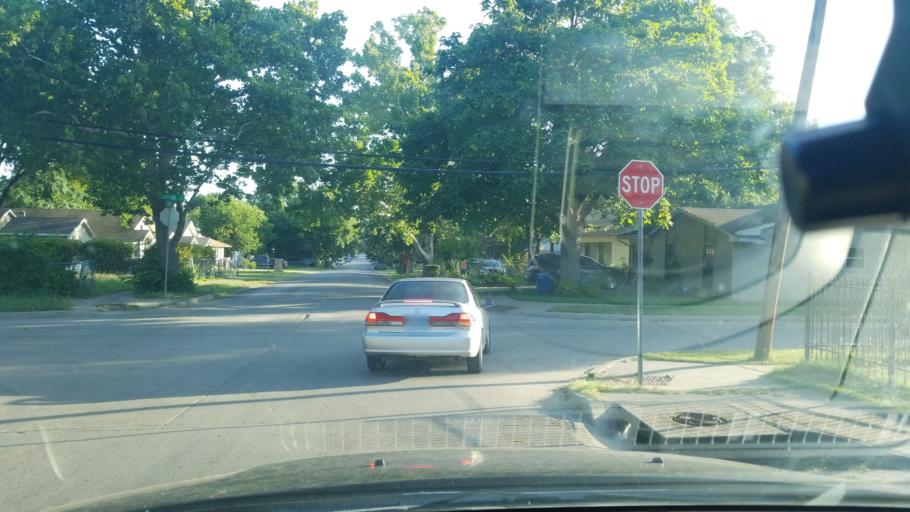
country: US
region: Texas
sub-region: Dallas County
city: Cockrell Hill
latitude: 32.7148
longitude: -96.8217
